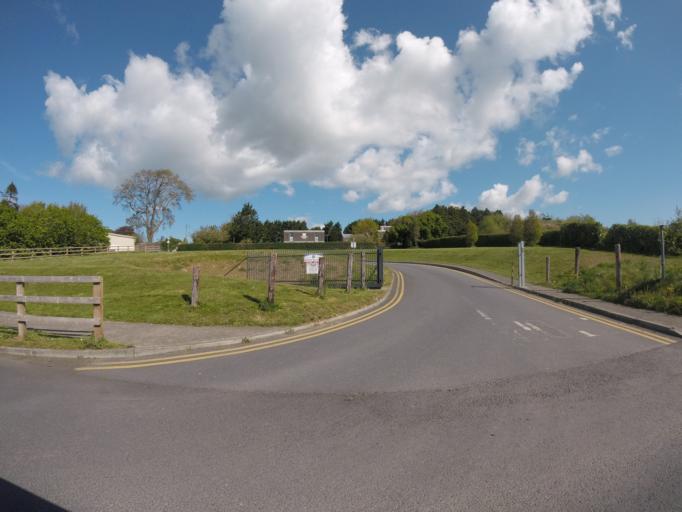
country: IE
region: Munster
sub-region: Waterford
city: Waterford
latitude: 52.2729
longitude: -7.0902
